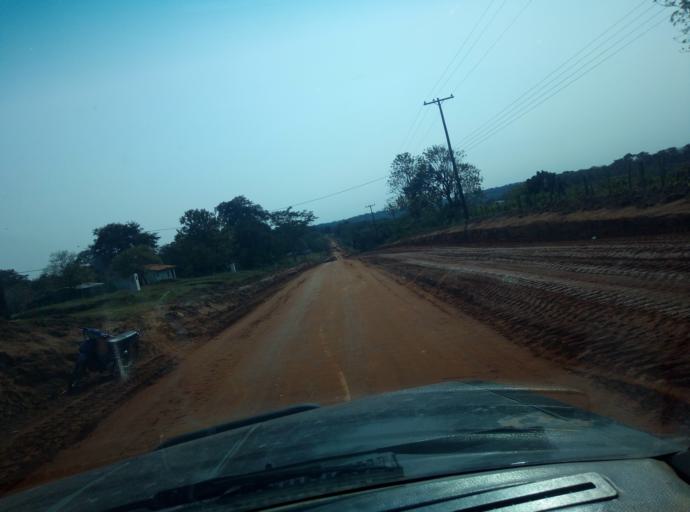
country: PY
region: Caaguazu
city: Carayao
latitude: -25.3135
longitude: -56.3268
